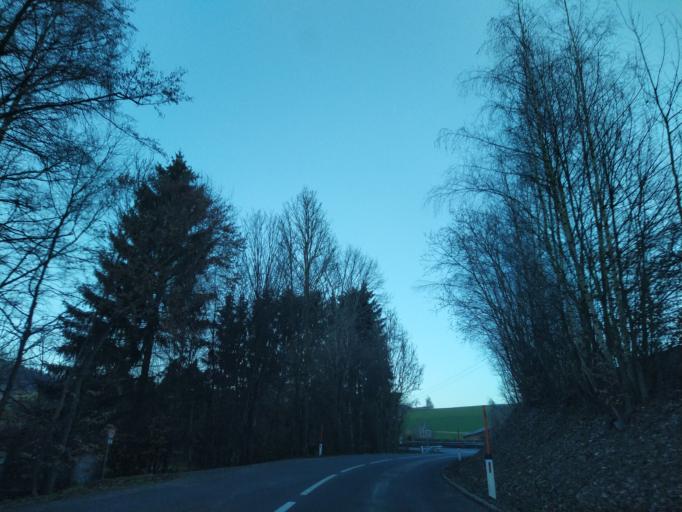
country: AT
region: Upper Austria
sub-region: Politischer Bezirk Urfahr-Umgebung
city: Kirchschlag bei Linz
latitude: 48.3932
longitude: 14.2887
